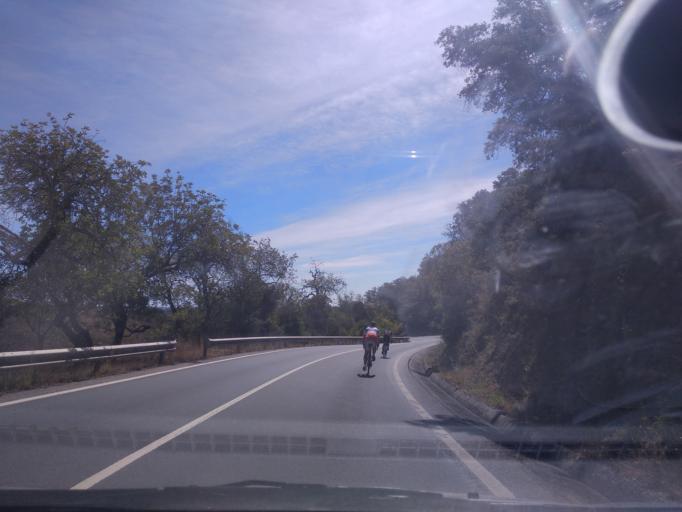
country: PT
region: Faro
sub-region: Sao Bras de Alportel
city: Sao Bras de Alportel
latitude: 37.1557
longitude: -7.8438
